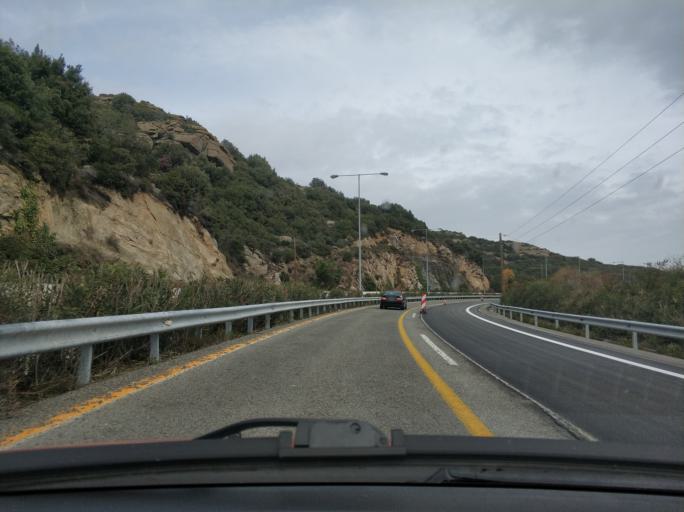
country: GR
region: East Macedonia and Thrace
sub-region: Nomos Kavalas
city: Palaio Tsifliki
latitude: 40.9139
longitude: 24.3597
